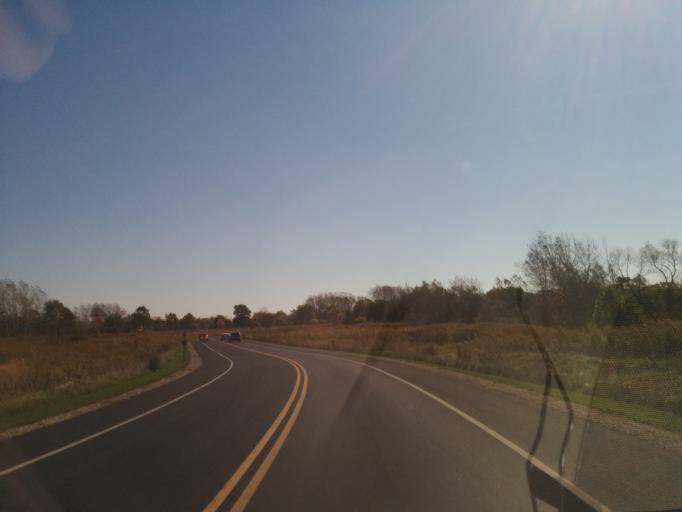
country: US
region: Illinois
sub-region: DuPage County
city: Carol Stream
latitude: 41.9568
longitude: -88.1279
